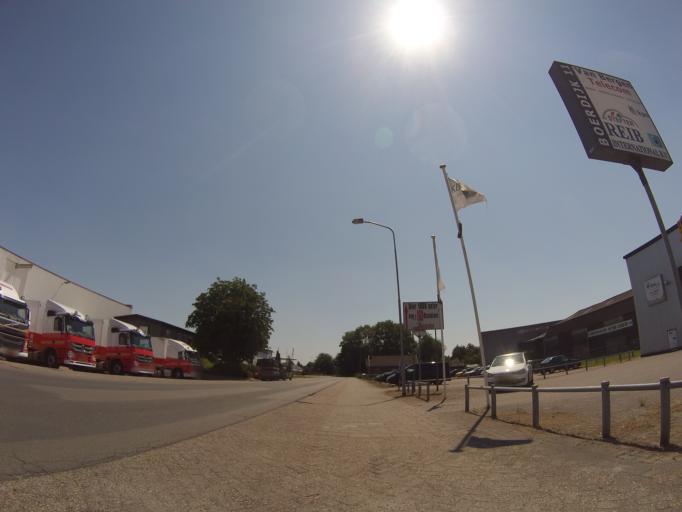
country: NL
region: Drenthe
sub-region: Gemeente Coevorden
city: Sleen
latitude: 52.7187
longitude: 6.8450
